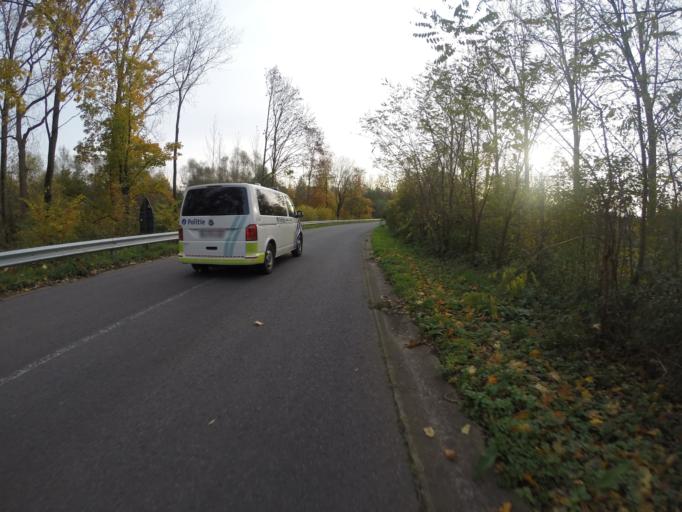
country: BE
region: Flanders
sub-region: Provincie Oost-Vlaanderen
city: Aalter
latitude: 51.0645
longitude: 3.4922
